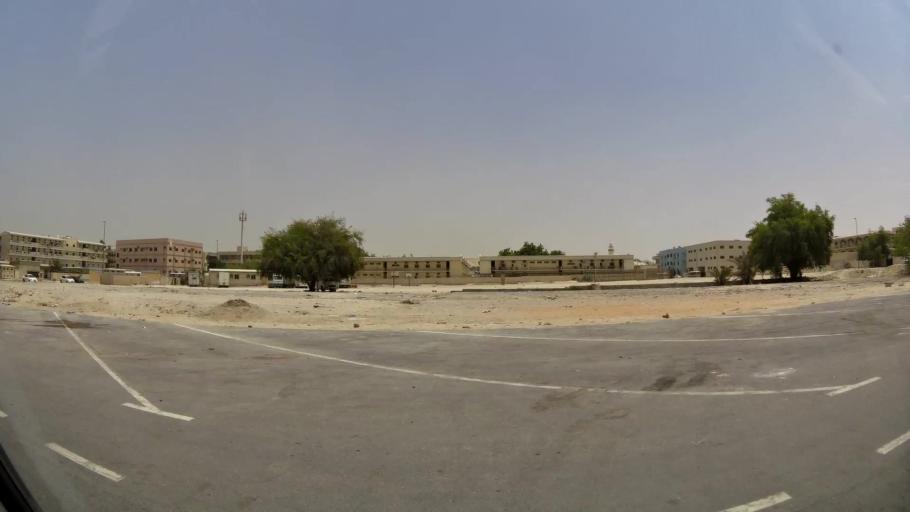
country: AE
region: Ash Shariqah
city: Sharjah
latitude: 25.2722
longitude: 55.4242
